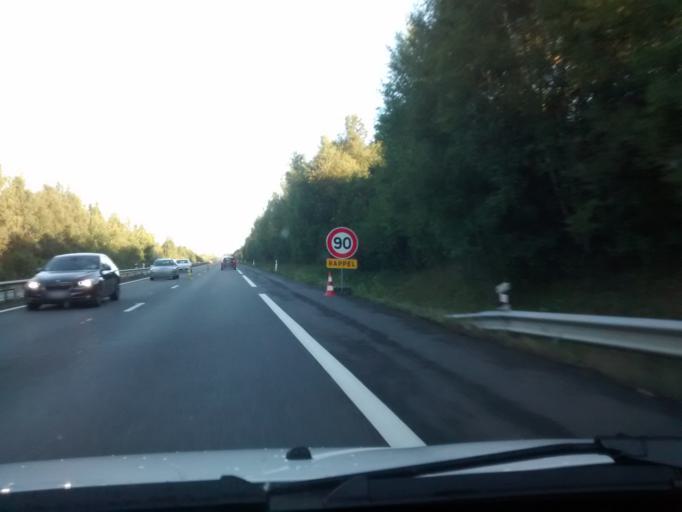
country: FR
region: Brittany
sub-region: Departement d'Ille-et-Vilaine
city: Saint-Domineuc
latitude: 48.3753
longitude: -1.8912
